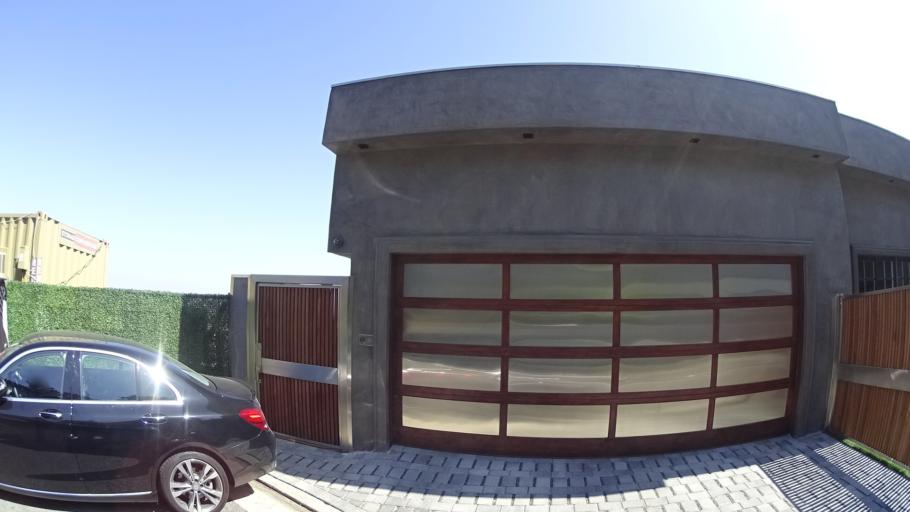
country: US
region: California
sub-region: Los Angeles County
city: West Hollywood
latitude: 34.0937
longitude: -118.3832
